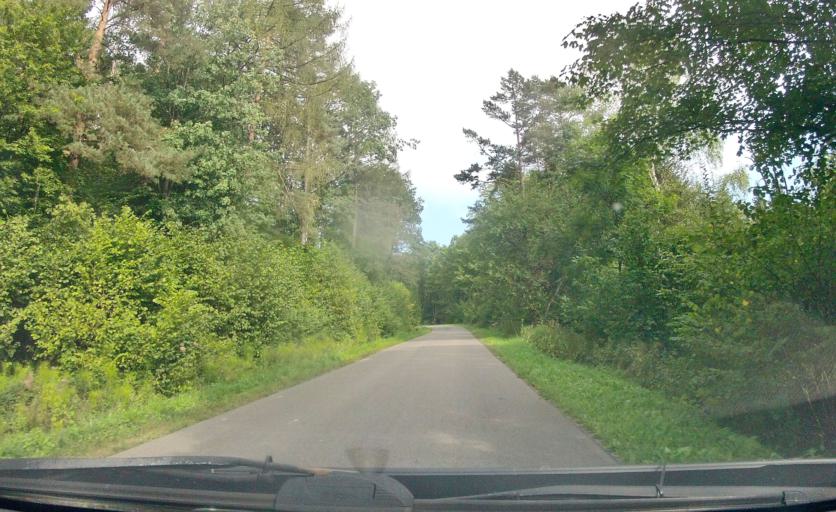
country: PL
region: Subcarpathian Voivodeship
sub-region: Powiat jasielski
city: Krempna
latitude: 49.4995
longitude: 21.5983
